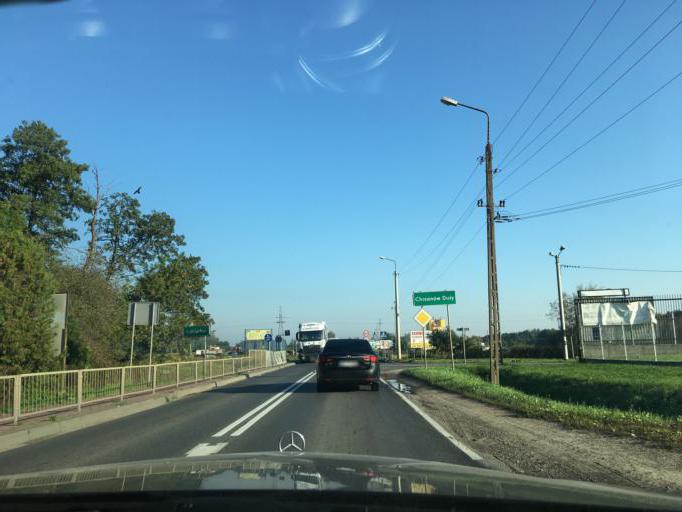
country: PL
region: Masovian Voivodeship
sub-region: Powiat grodziski
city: Grodzisk Mazowiecki
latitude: 52.1198
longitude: 20.6200
